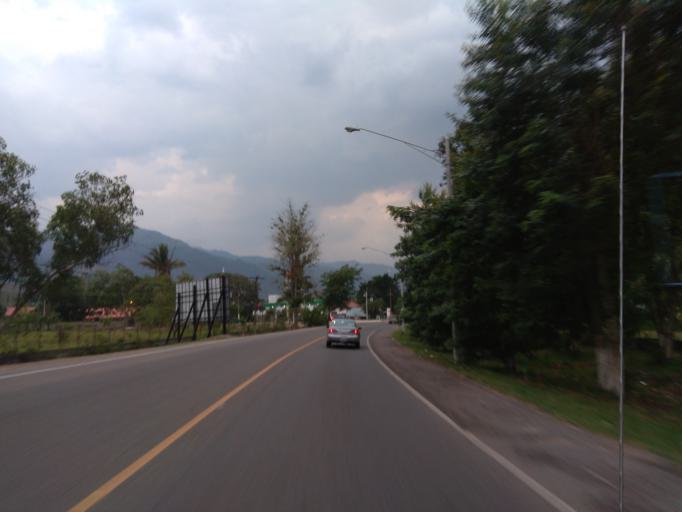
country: HN
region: Yoro
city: El Progreso
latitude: 15.3728
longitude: -87.8028
